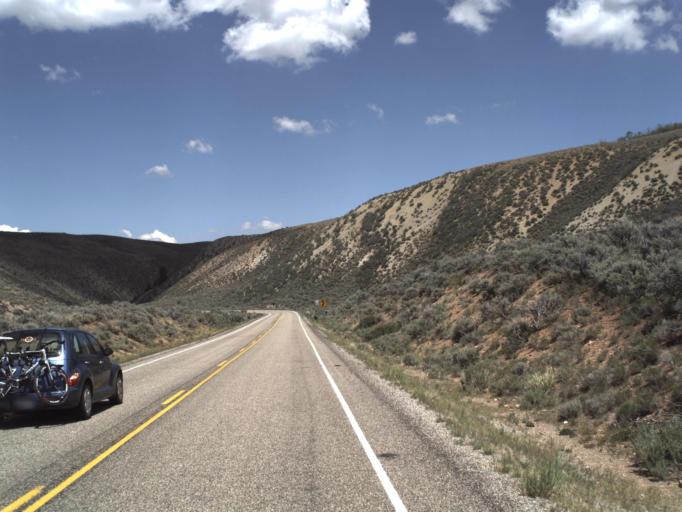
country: US
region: Utah
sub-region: Rich County
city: Randolph
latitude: 41.4937
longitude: -111.3307
